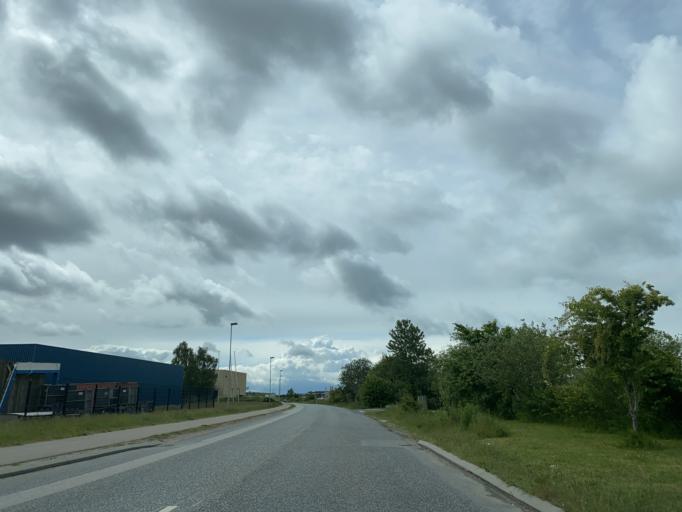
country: DK
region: Central Jutland
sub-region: Arhus Kommune
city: Stavtrup
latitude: 56.1875
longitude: 10.1294
